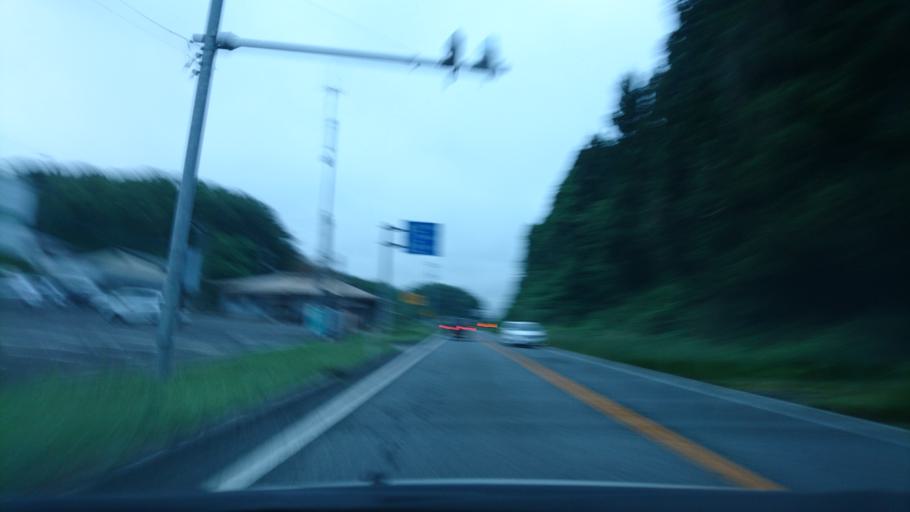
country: JP
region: Iwate
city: Ichinoseki
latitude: 38.8836
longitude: 141.1182
